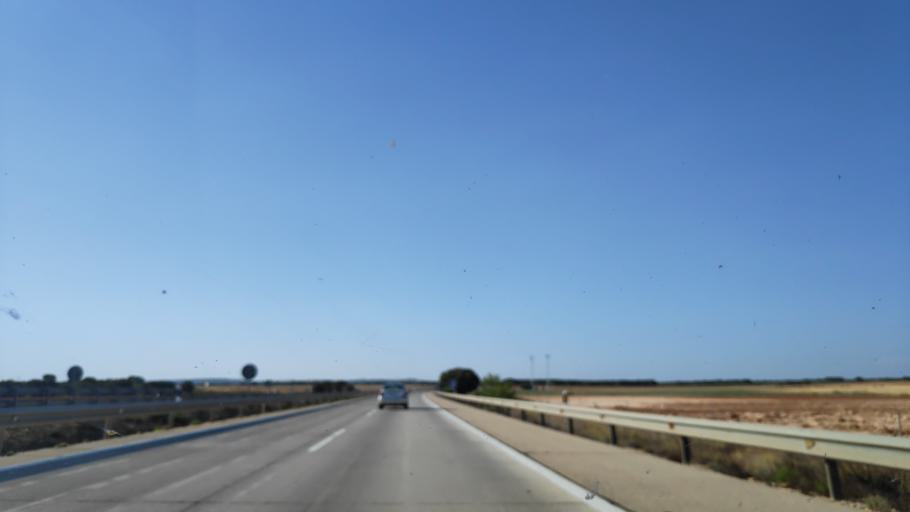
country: ES
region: Castille-La Mancha
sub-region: Provincia de Cuenca
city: Casas de Guijarro
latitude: 39.3153
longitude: -2.2035
